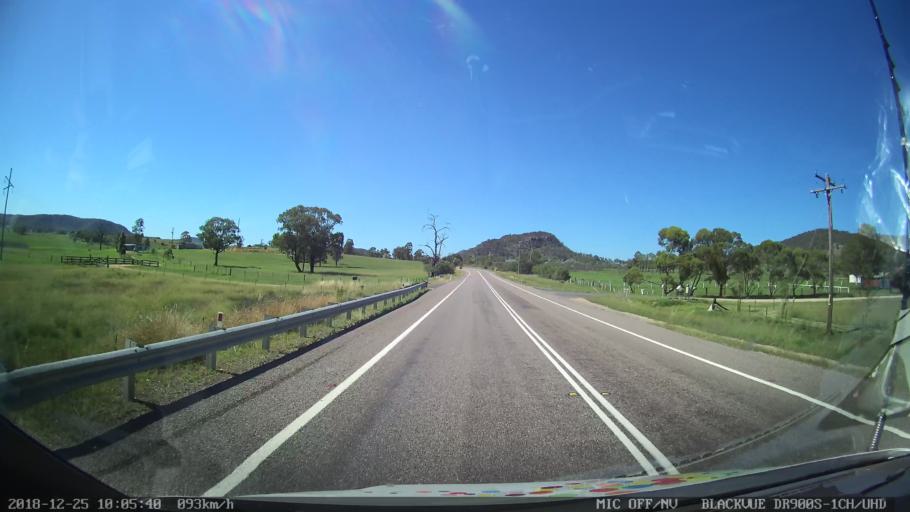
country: AU
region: New South Wales
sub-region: Upper Hunter Shire
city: Merriwa
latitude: -32.2502
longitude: 150.4868
